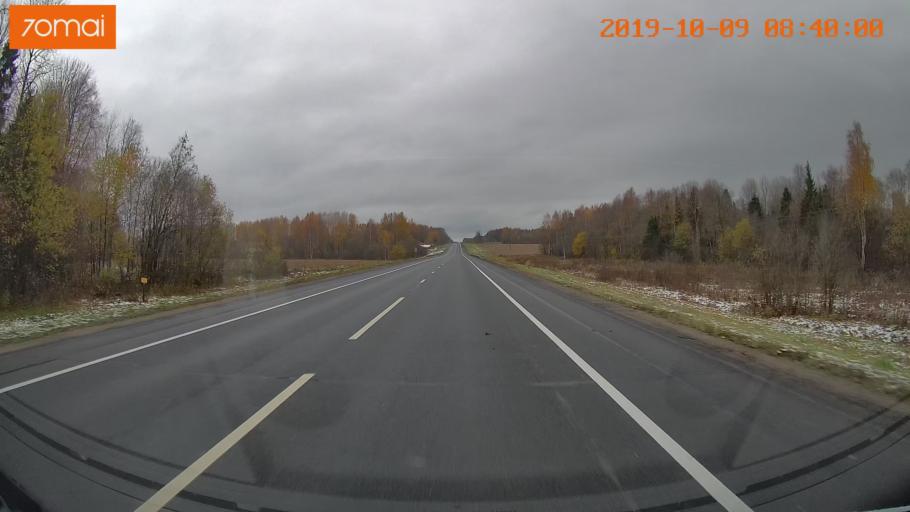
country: RU
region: Vologda
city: Gryazovets
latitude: 58.9800
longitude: 40.1459
